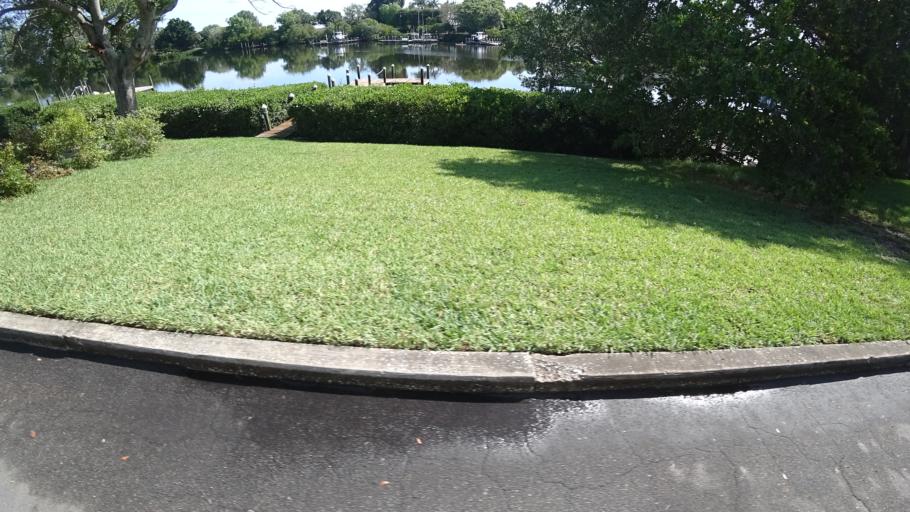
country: US
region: Florida
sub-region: Manatee County
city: West Bradenton
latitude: 27.5062
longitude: -82.6158
